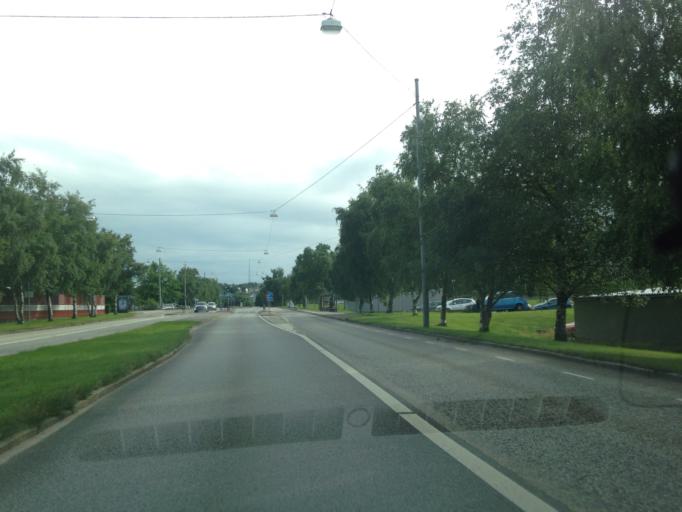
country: SE
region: Vaestra Goetaland
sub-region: Goteborg
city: Goeteborg
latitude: 57.7468
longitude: 11.9782
